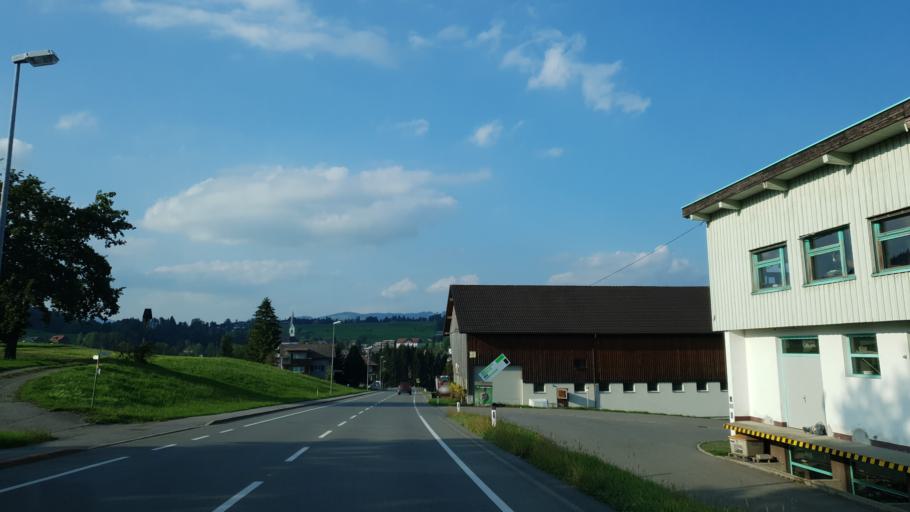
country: AT
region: Vorarlberg
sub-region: Politischer Bezirk Bregenz
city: Egg
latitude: 47.4231
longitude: 9.8980
